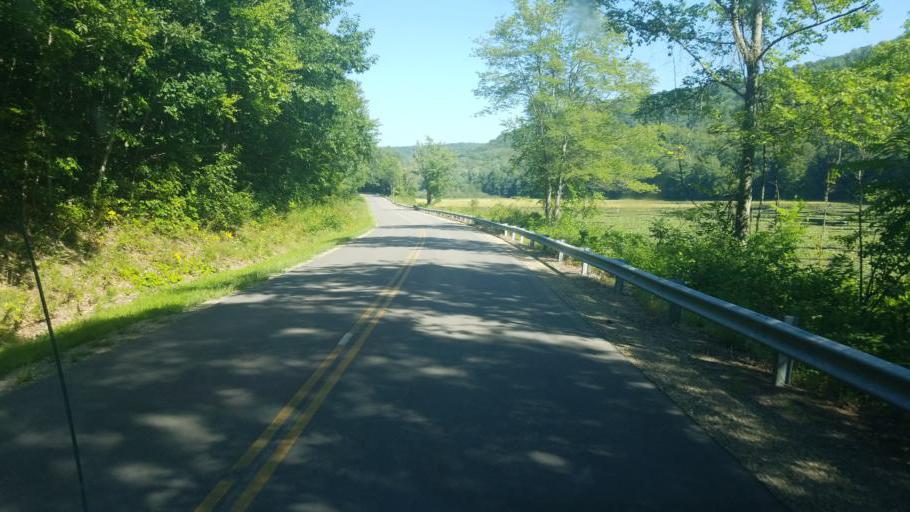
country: US
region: New York
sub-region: Allegany County
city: Wellsville
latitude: 42.0222
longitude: -77.9744
